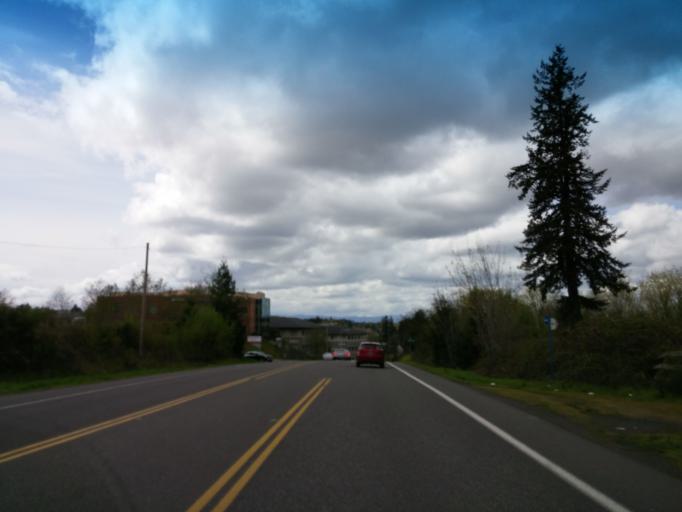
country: US
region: Oregon
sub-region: Washington County
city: Cedar Hills
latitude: 45.5171
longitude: -122.7954
